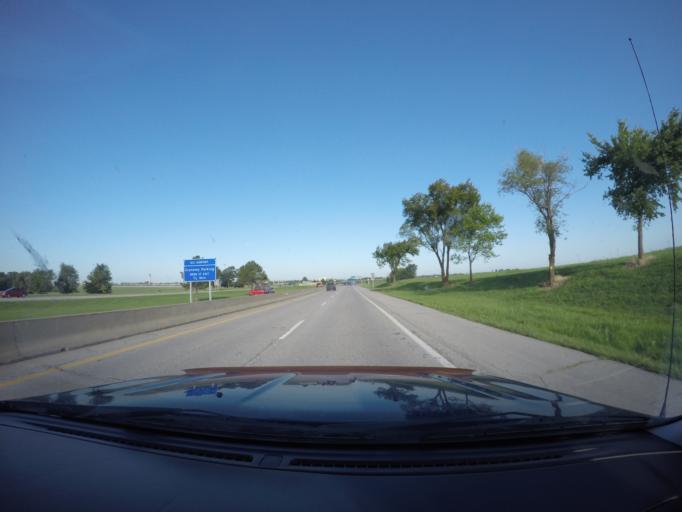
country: US
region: Missouri
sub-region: Platte County
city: Weatherby Lake
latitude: 39.3113
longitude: -94.6939
